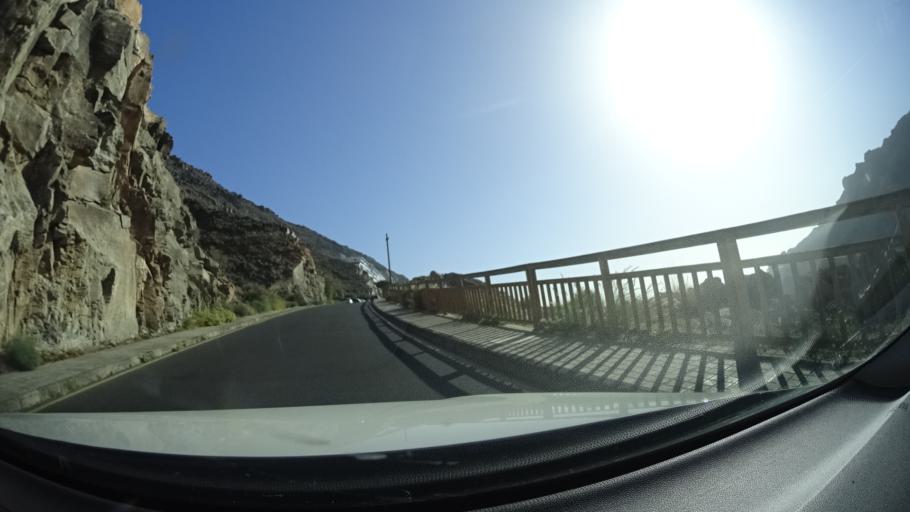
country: ES
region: Canary Islands
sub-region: Provincia de Las Palmas
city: Puerto Rico
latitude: 27.8183
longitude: -15.7497
